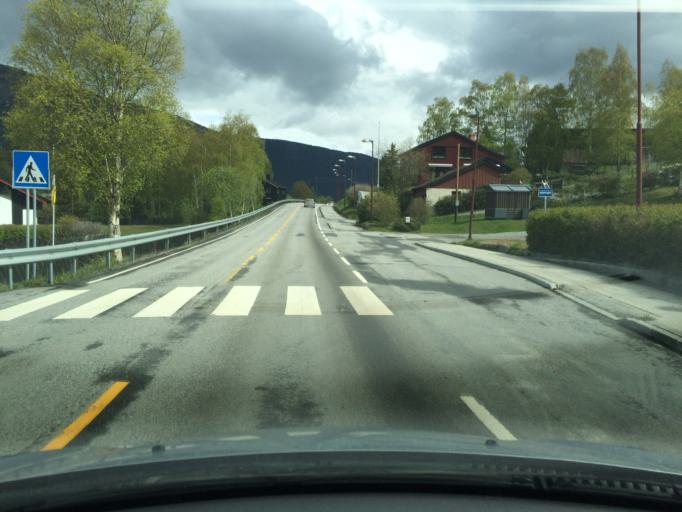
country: NO
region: Oppland
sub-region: Lom
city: Fossbergom
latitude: 61.8334
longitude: 8.5590
